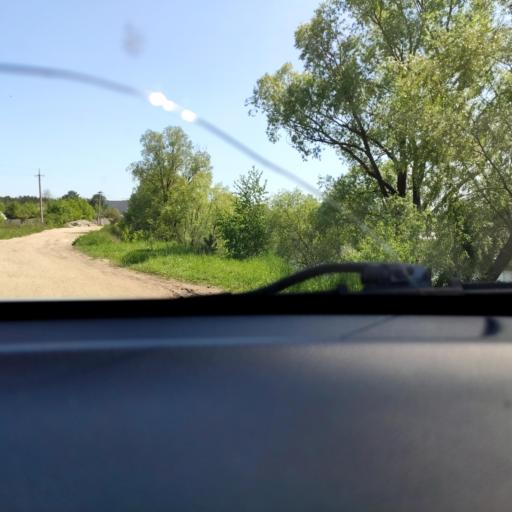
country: RU
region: Tatarstan
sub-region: Gorod Kazan'
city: Kazan
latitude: 55.8638
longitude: 49.1960
